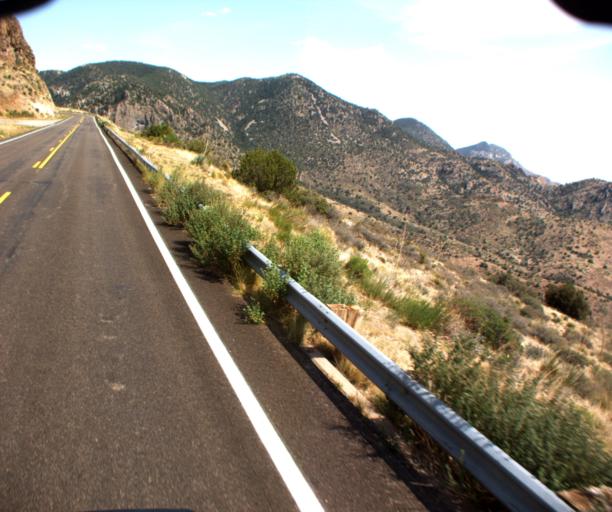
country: US
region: Arizona
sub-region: Greenlee County
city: Clifton
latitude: 33.0507
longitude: -109.0984
